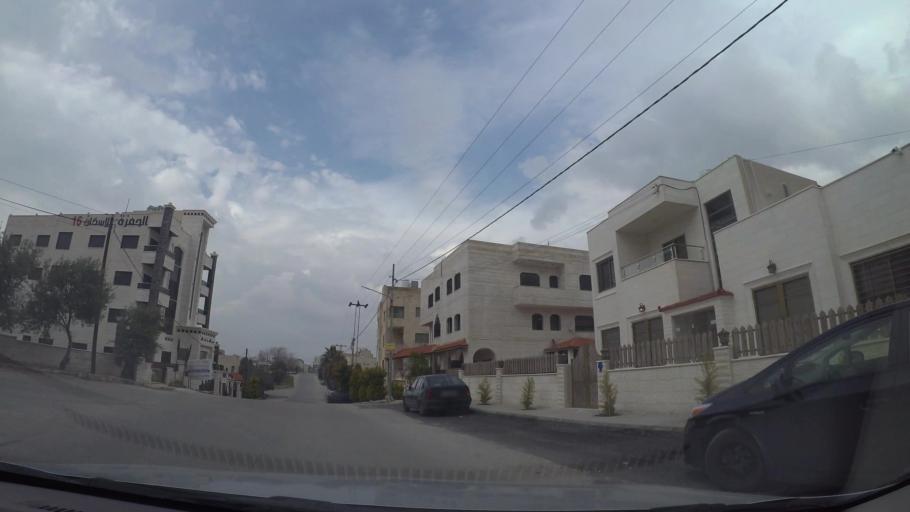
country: JO
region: Amman
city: Umm as Summaq
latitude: 31.8820
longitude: 35.8571
